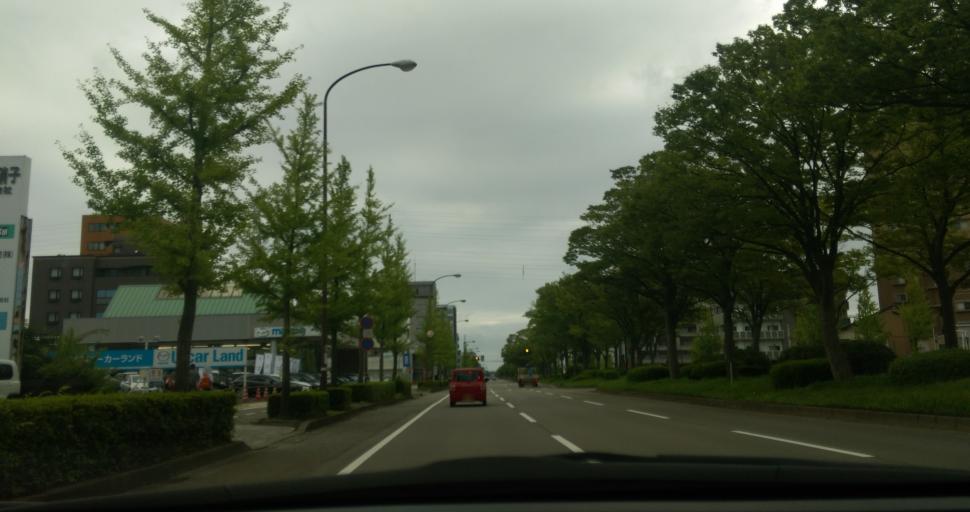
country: JP
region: Ishikawa
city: Kanazawa-shi
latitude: 36.5842
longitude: 136.6385
